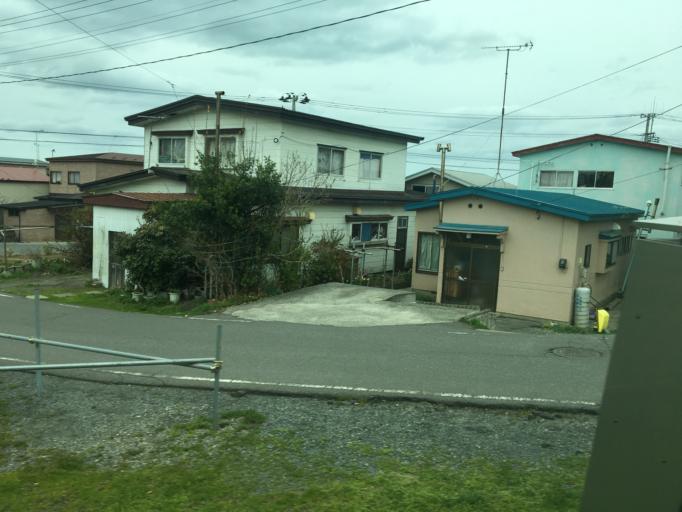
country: JP
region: Aomori
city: Shimokizukuri
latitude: 40.7796
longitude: 140.2253
